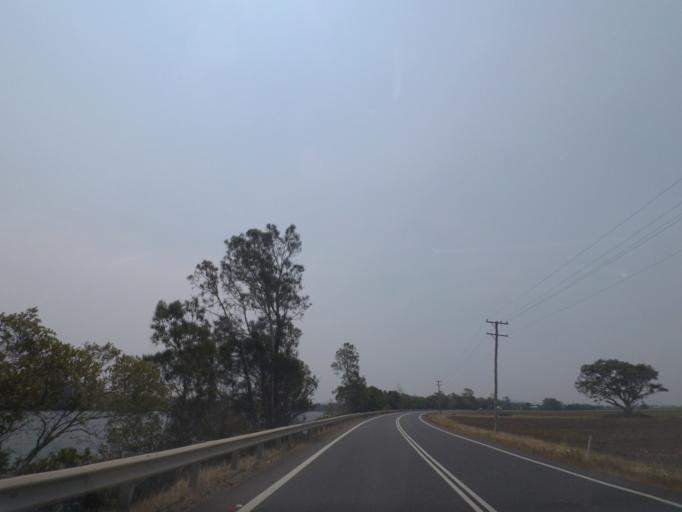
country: AU
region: New South Wales
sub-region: Richmond Valley
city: Evans Head
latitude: -28.9749
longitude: 153.4611
